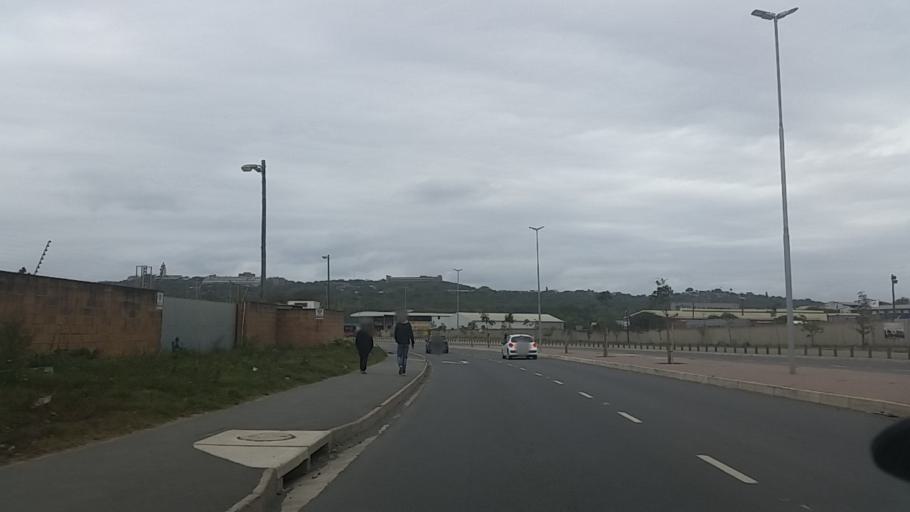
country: ZA
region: KwaZulu-Natal
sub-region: eThekwini Metropolitan Municipality
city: Berea
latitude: -29.8628
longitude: 30.9611
